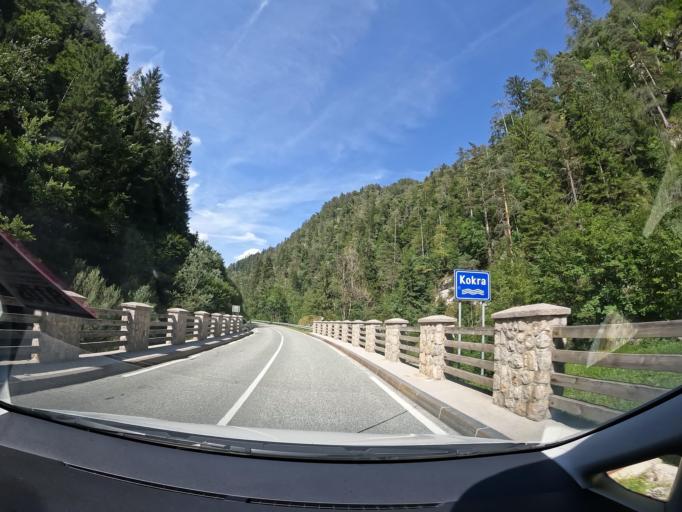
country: SI
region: Trzic
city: Trzic
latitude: 46.4274
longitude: 14.2696
